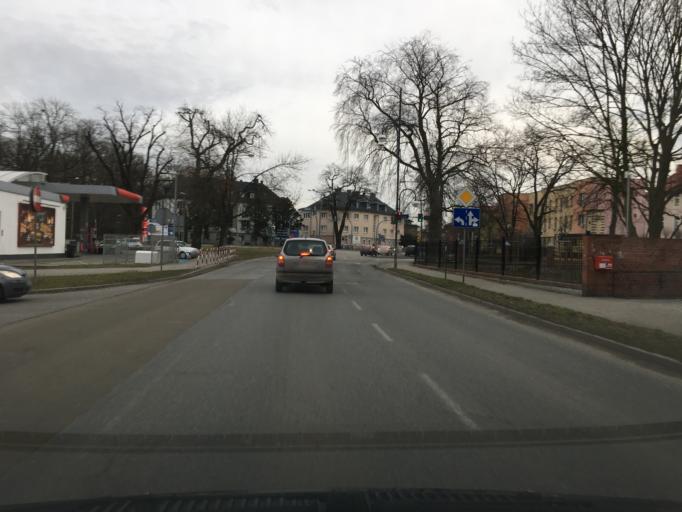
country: PL
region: Opole Voivodeship
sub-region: Powiat kedzierzynsko-kozielski
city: Kozle
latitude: 50.3360
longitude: 18.1465
